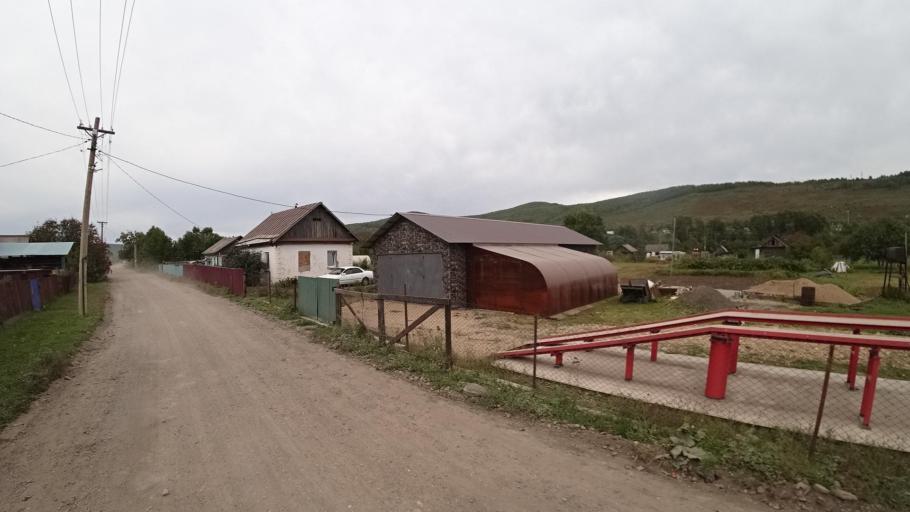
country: RU
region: Jewish Autonomous Oblast
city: Khingansk
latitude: 49.0321
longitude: 131.0491
